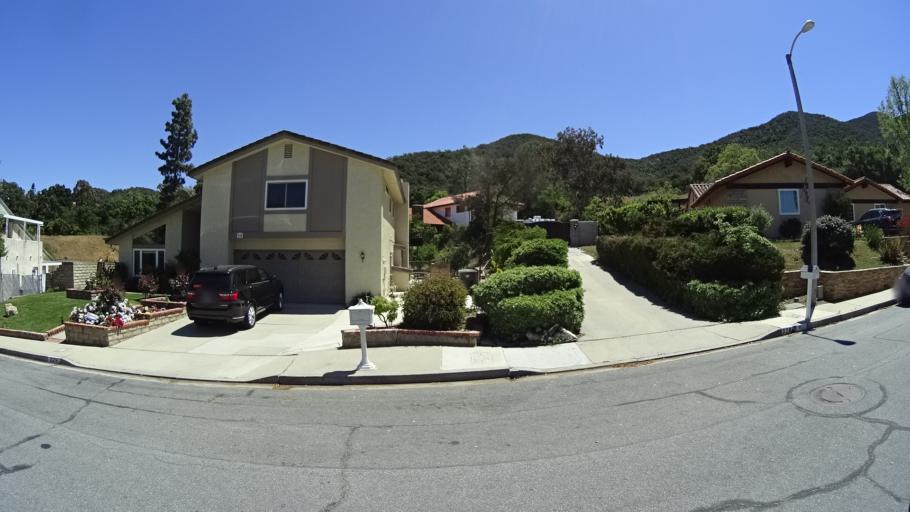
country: US
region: California
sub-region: Ventura County
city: Casa Conejo
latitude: 34.1733
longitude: -118.8982
